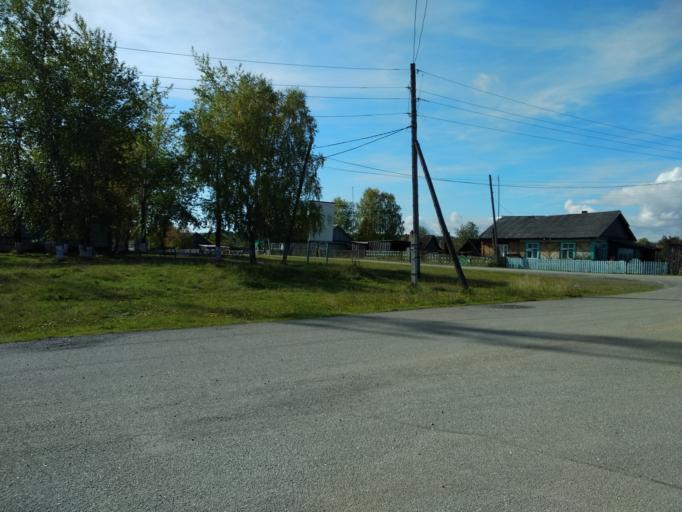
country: RU
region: Sverdlovsk
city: Karpinsk
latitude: 59.9324
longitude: 59.8105
